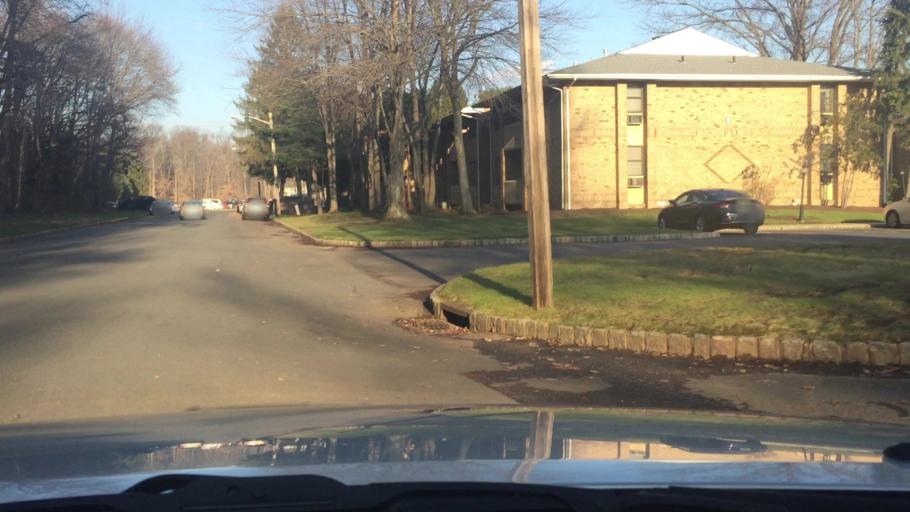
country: US
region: New Jersey
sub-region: Middlesex County
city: Kendall Park
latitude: 40.4373
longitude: -74.5212
